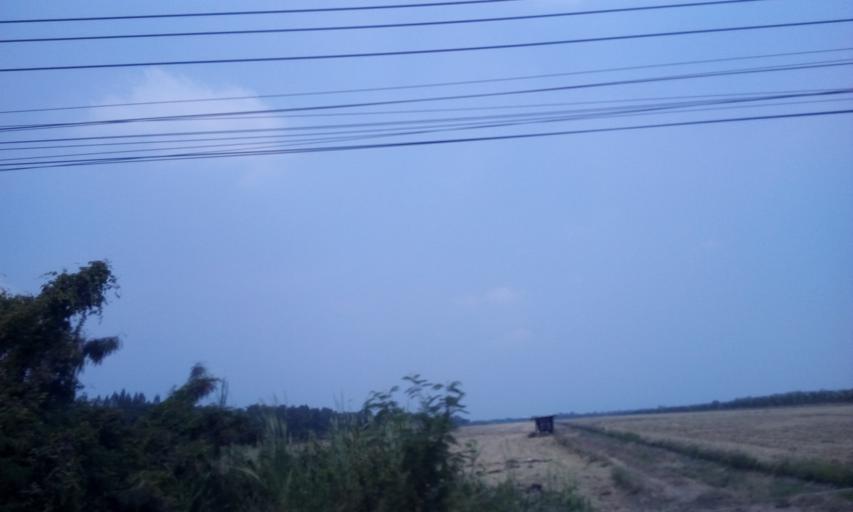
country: TH
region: Bangkok
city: Nong Chok
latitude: 13.9603
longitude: 100.8882
